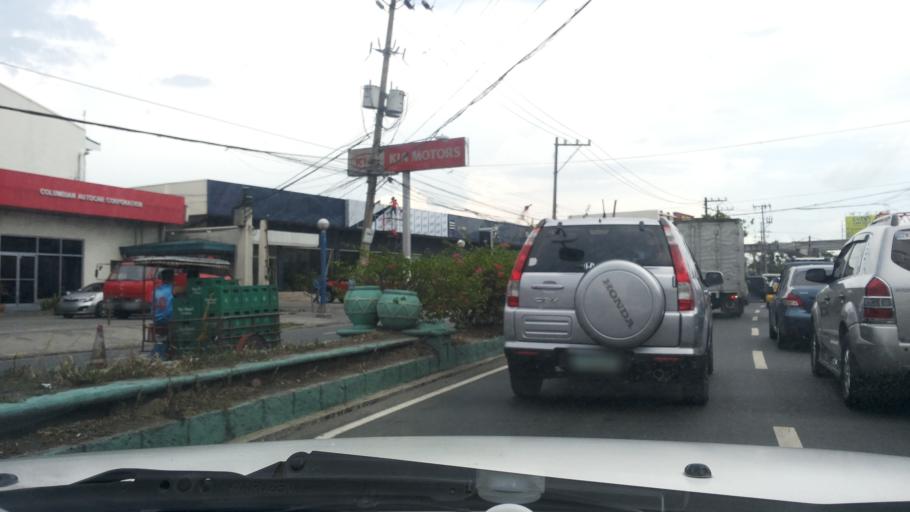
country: PH
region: Metro Manila
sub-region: Makati City
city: Makati City
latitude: 14.5297
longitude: 121.0046
